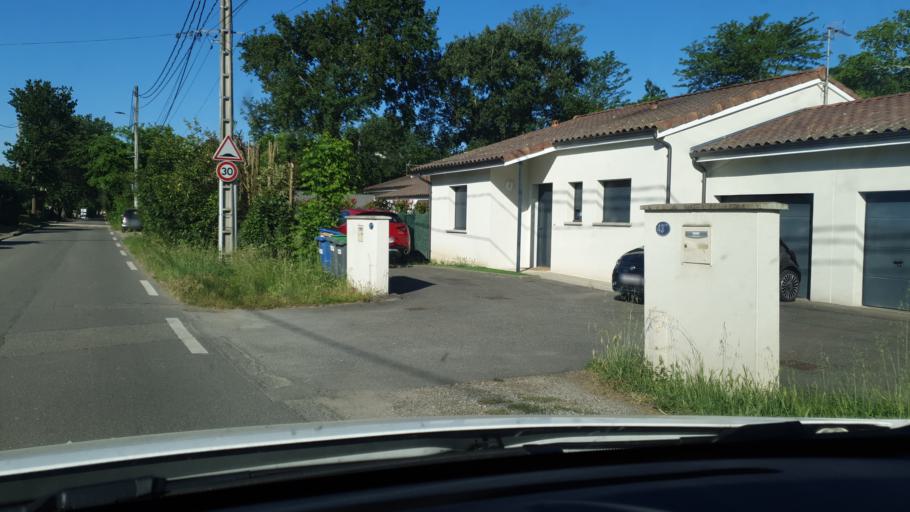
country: FR
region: Midi-Pyrenees
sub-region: Departement de la Haute-Garonne
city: Saint-Orens-de-Gameville
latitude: 43.5592
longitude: 1.5085
